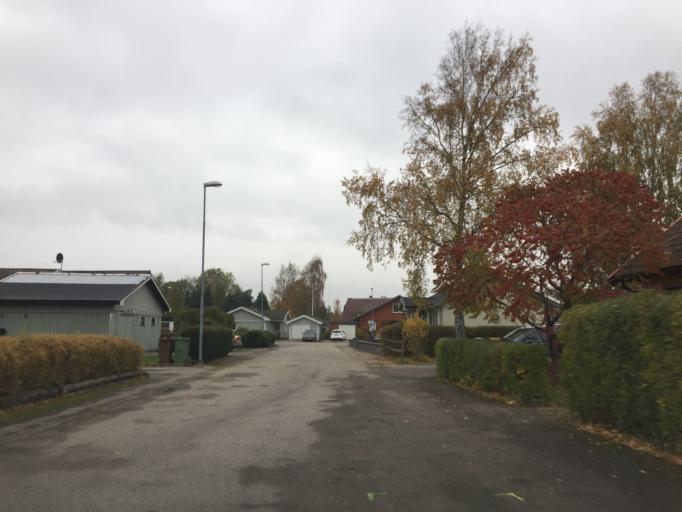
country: SE
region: Vaestra Goetaland
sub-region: Trollhattan
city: Sjuntorp
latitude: 58.1822
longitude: 12.2199
